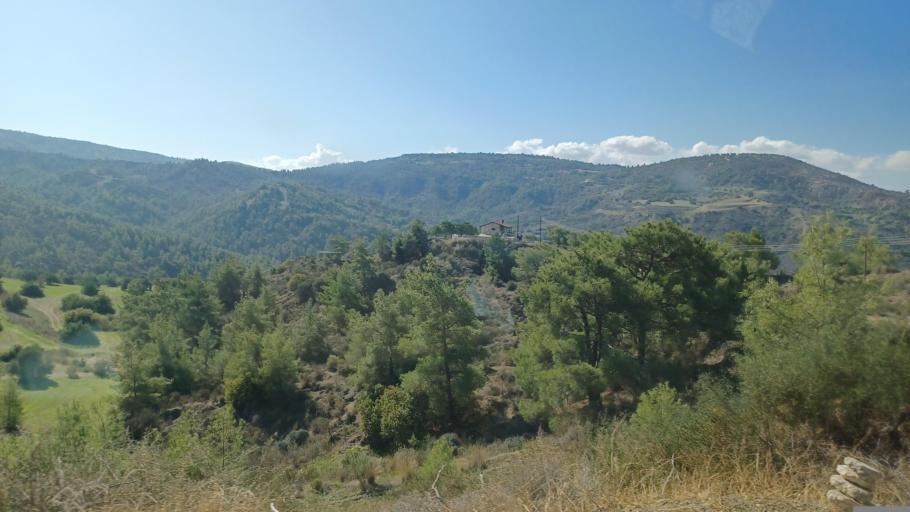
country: CY
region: Pafos
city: Polis
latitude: 35.0350
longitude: 32.4953
